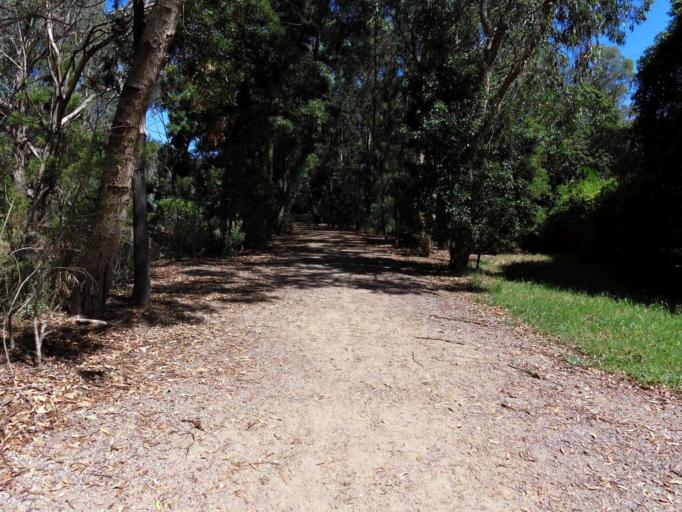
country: AU
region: Victoria
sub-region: Maroondah
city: Croydon North
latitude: -37.7762
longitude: 145.3023
